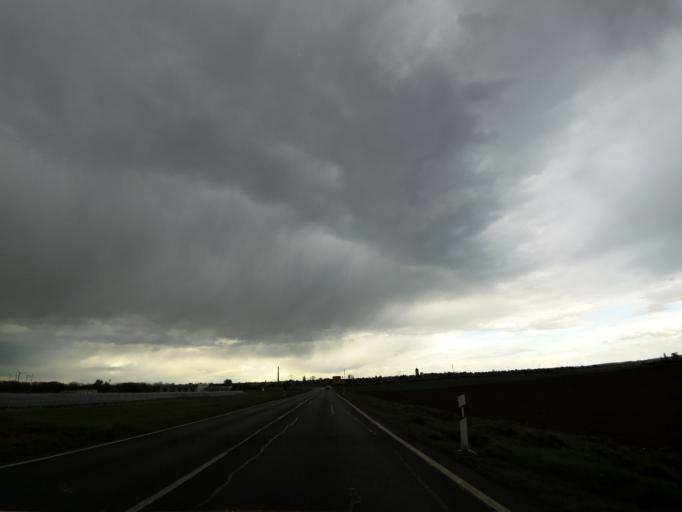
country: DE
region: Saxony-Anhalt
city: Westeregeln
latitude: 51.9407
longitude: 11.4000
